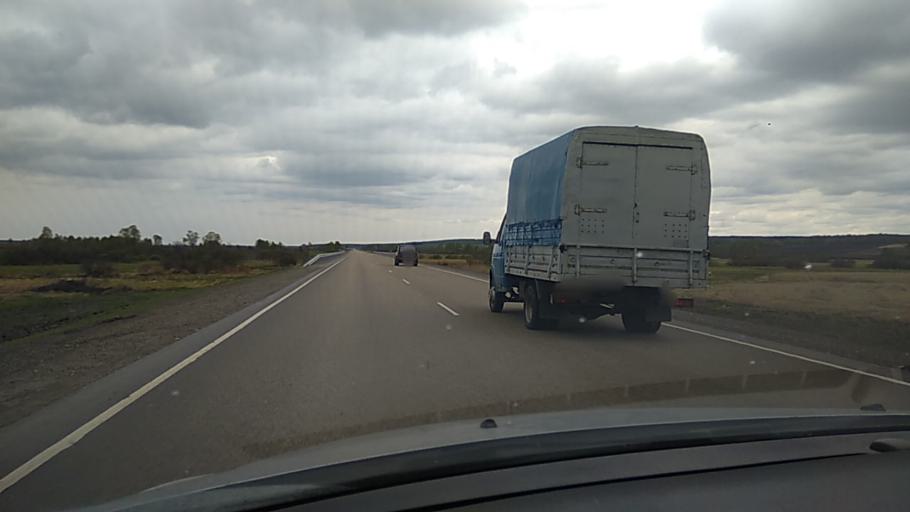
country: RU
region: Kurgan
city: Kataysk
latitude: 56.2983
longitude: 62.4573
